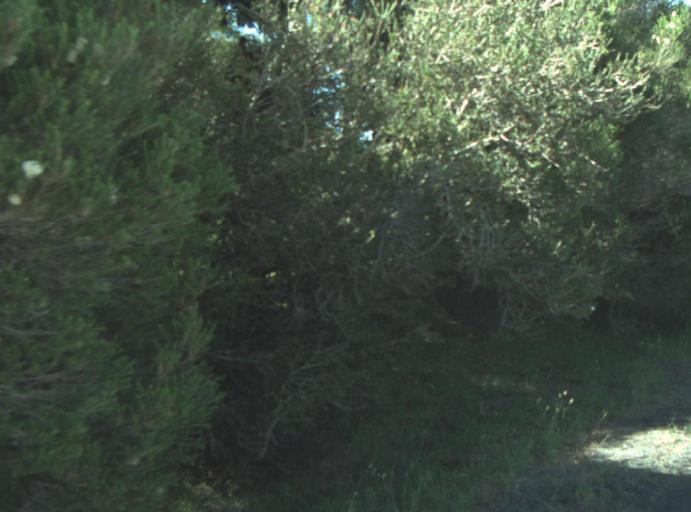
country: AU
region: Victoria
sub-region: Greater Geelong
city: Clifton Springs
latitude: -38.2473
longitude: 144.5684
